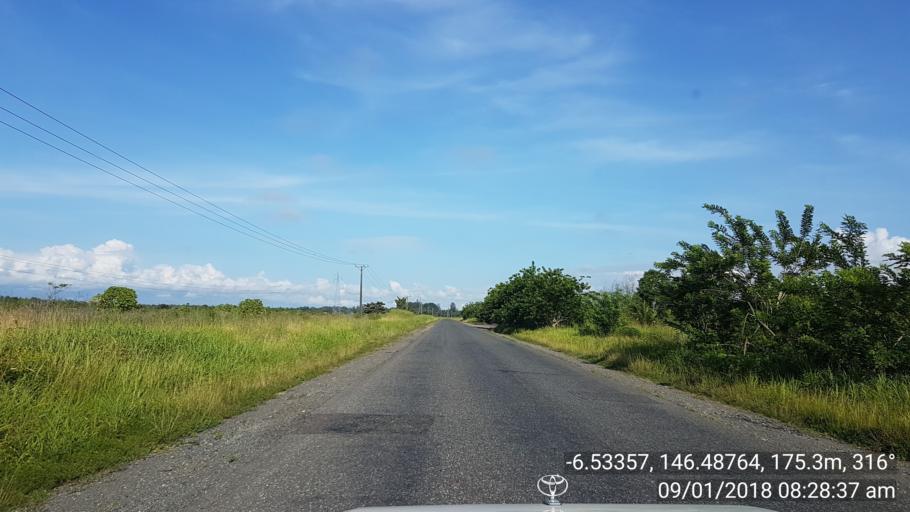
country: PG
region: Morobe
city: Lae
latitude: -6.5338
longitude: 146.4878
